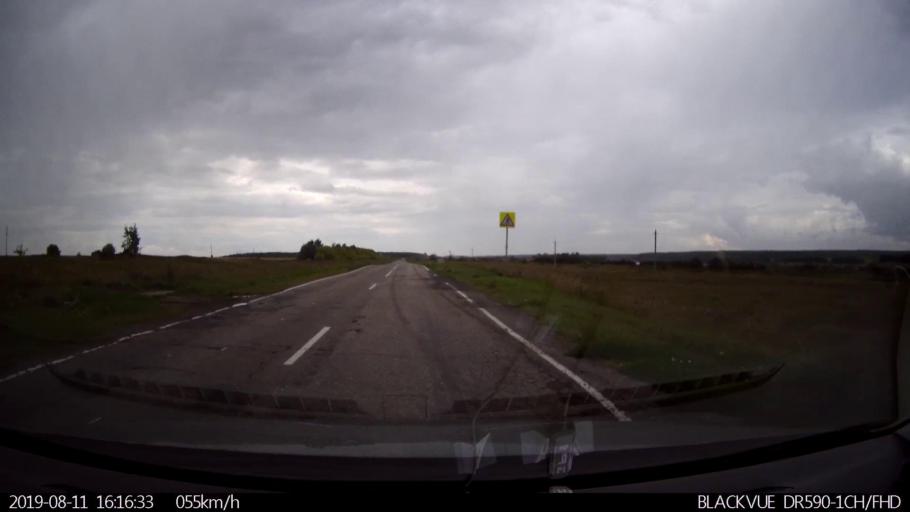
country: RU
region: Ulyanovsk
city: Mayna
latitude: 54.0419
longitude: 47.6208
